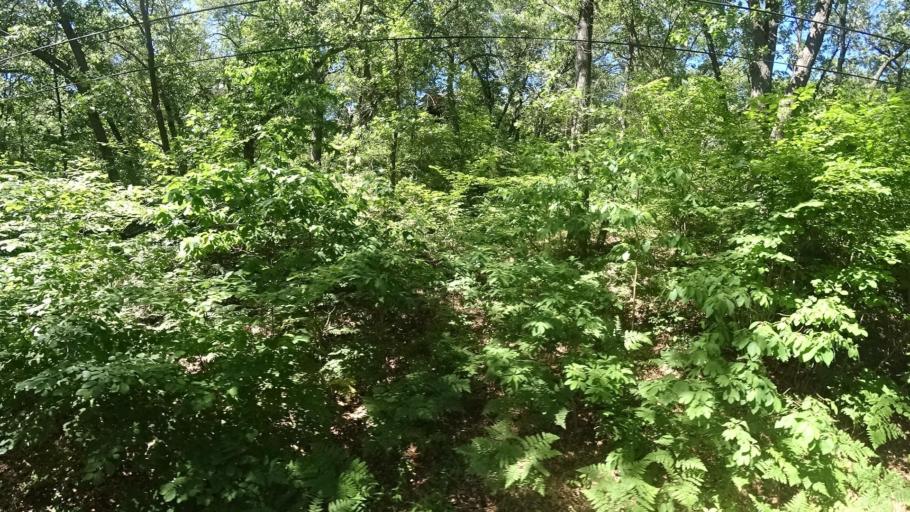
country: US
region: Indiana
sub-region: Porter County
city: Porter
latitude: 41.6550
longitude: -87.0712
